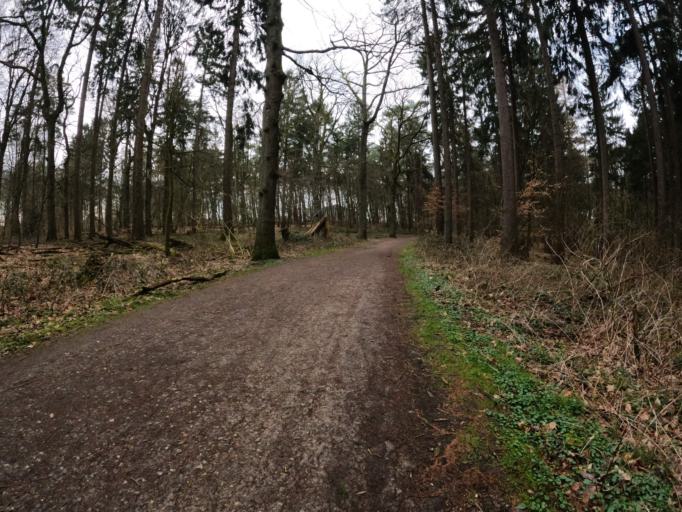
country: DE
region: Hamburg
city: Harburg
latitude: 53.4587
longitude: 9.9329
